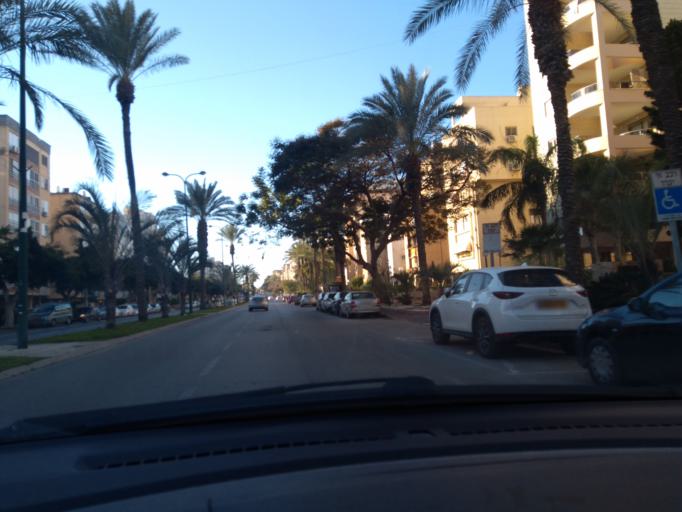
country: IL
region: Central District
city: Netanya
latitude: 32.3404
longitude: 34.8599
